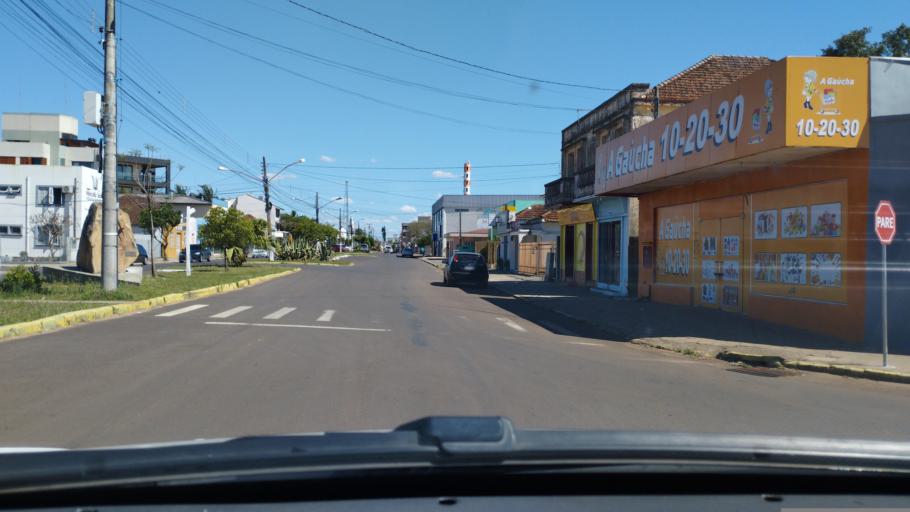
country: BR
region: Rio Grande do Sul
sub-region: Tupancireta
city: Tupancireta
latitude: -29.0772
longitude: -53.8385
